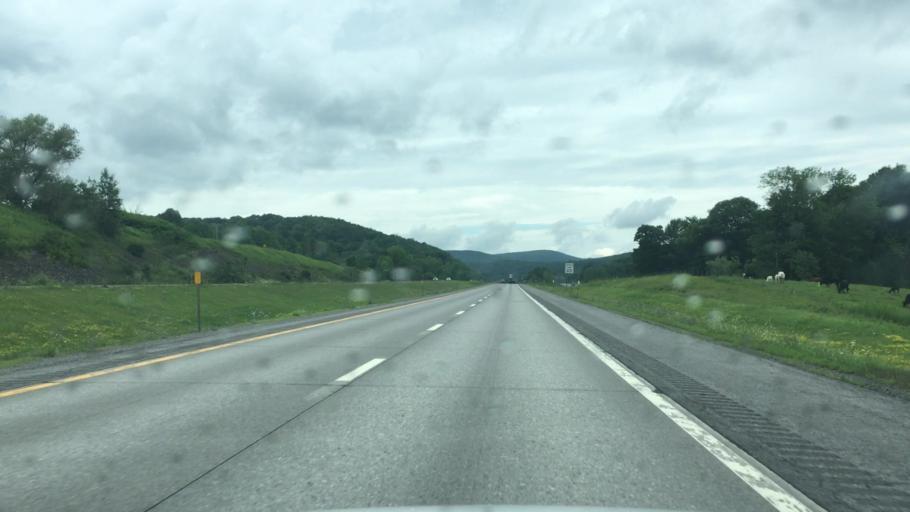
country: US
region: New York
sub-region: Schoharie County
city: Cobleskill
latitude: 42.6422
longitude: -74.5820
